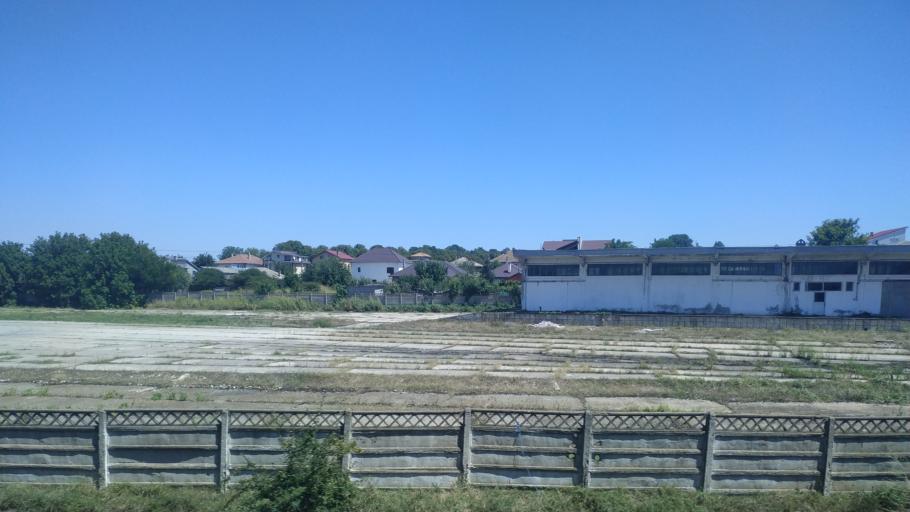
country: RO
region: Constanta
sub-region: Oras Murfatlar
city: Murfatlar
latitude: 44.1792
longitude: 28.4000
